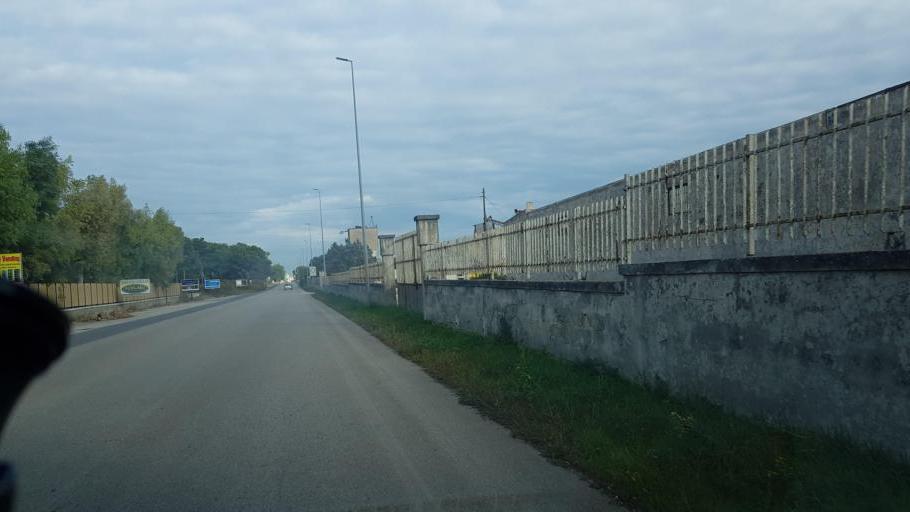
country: IT
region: Apulia
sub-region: Provincia di Brindisi
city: Francavilla Fontana
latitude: 40.5330
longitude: 17.5325
